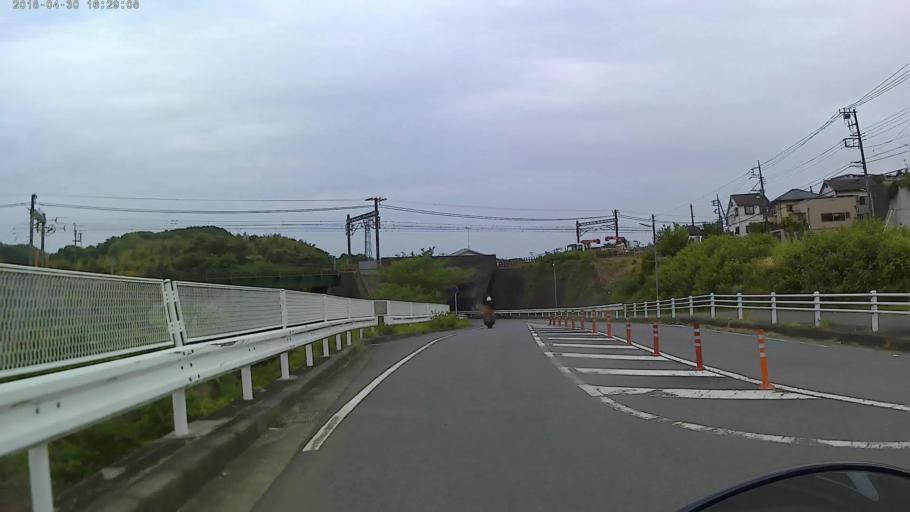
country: JP
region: Kanagawa
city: Zama
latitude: 35.4597
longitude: 139.4052
